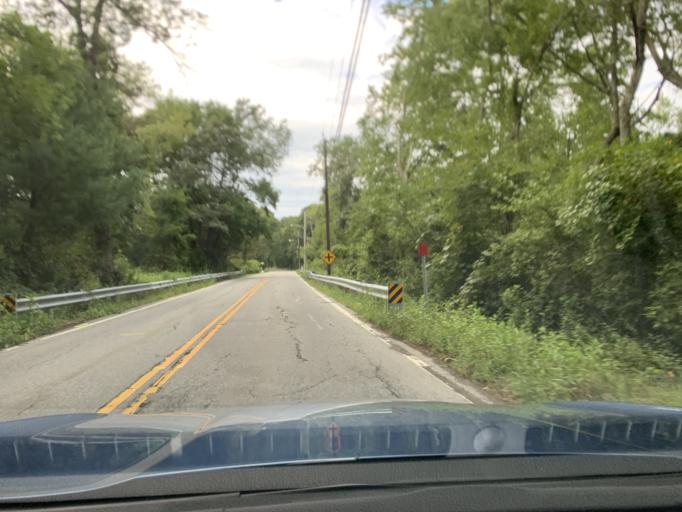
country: US
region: Rhode Island
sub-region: Kent County
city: East Greenwich
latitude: 41.6222
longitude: -71.4458
